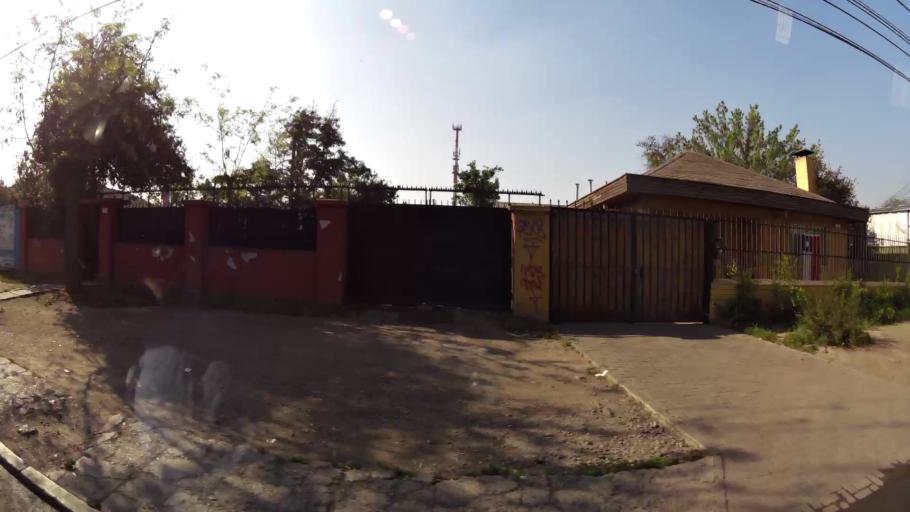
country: CL
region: Santiago Metropolitan
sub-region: Provincia de Santiago
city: Santiago
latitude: -33.3843
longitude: -70.6756
